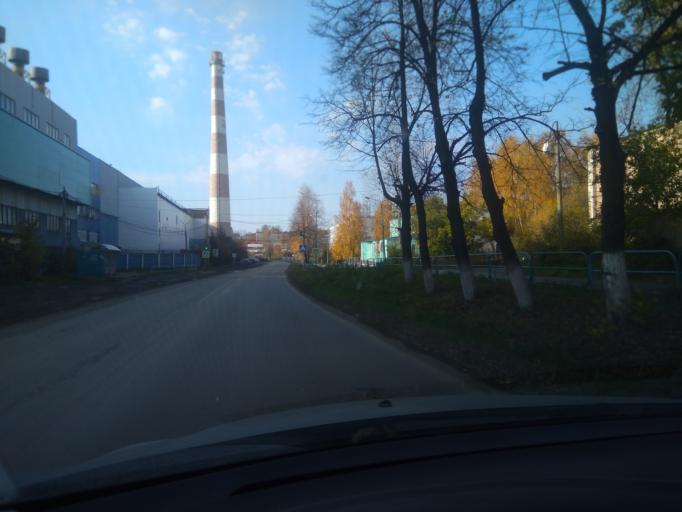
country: RU
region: Sverdlovsk
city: Nizhniye Sergi
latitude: 56.6655
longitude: 59.3111
